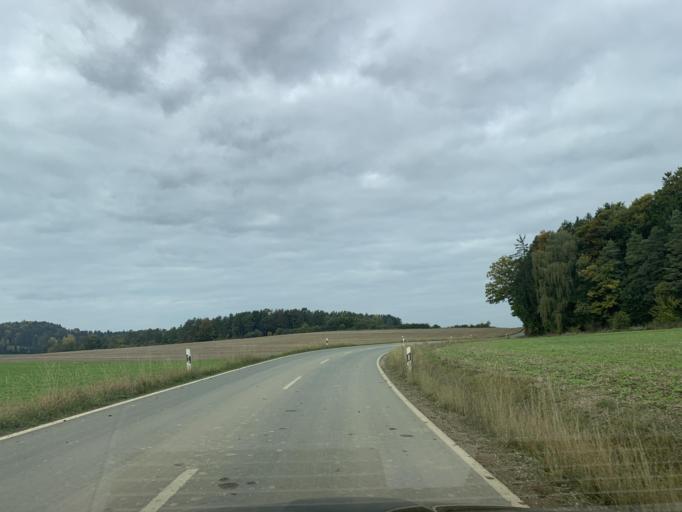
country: DE
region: Bavaria
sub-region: Upper Franconia
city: Unterleinleiter
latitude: 49.8470
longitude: 11.2385
